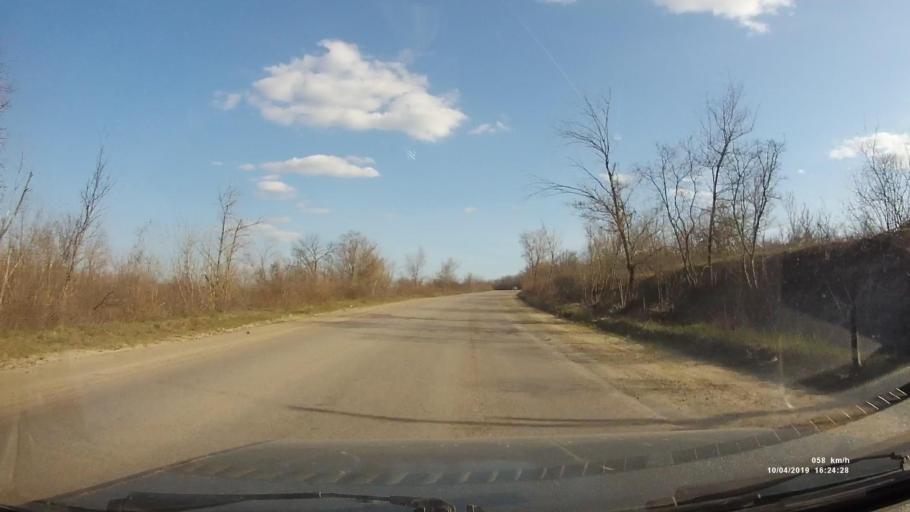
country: RU
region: Rostov
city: Staraya Stanitsa
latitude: 48.2994
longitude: 40.3151
